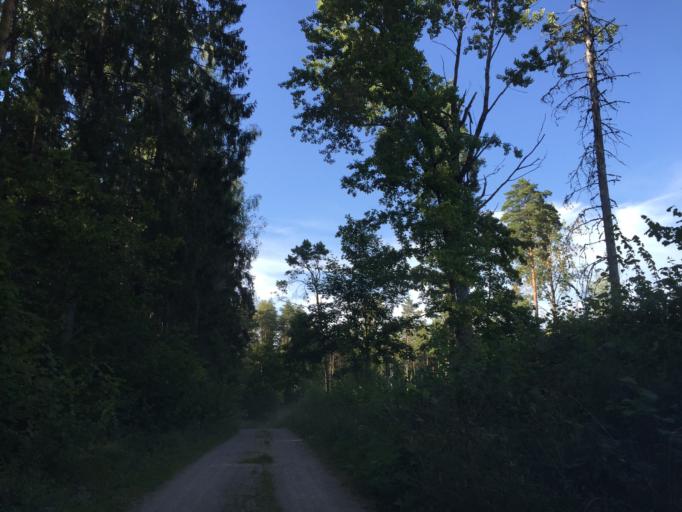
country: LT
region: Panevezys
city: Rokiskis
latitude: 55.8241
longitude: 25.8962
